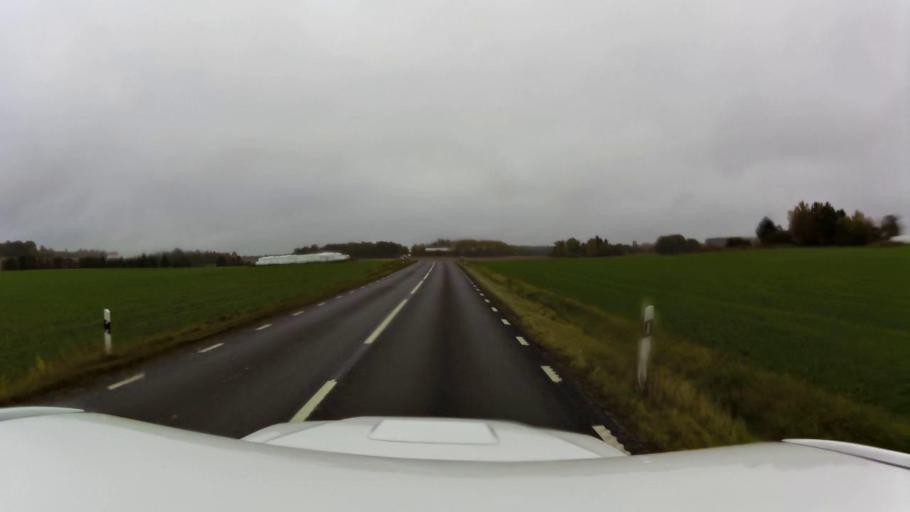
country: SE
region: OEstergoetland
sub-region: Linkopings Kommun
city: Linghem
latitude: 58.3909
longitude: 15.7767
